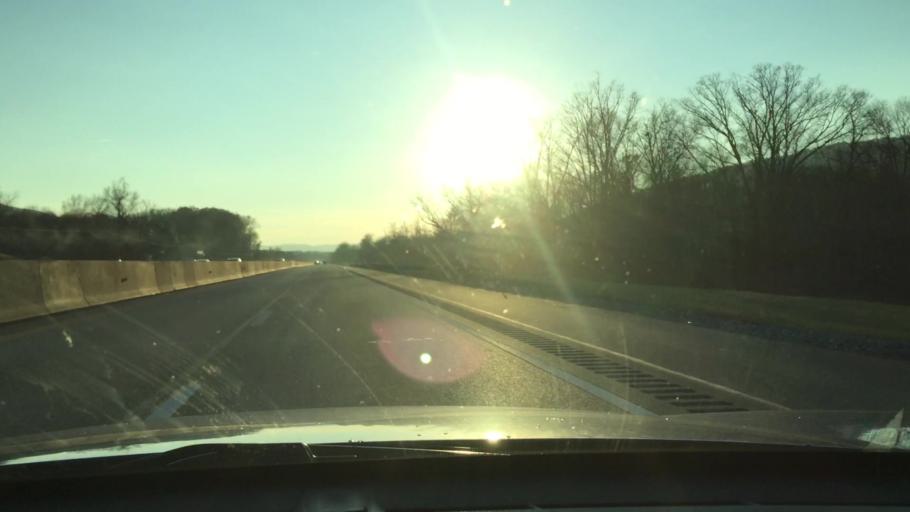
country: US
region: Pennsylvania
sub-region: Franklin County
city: Doylestown
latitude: 40.1454
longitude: -77.7216
